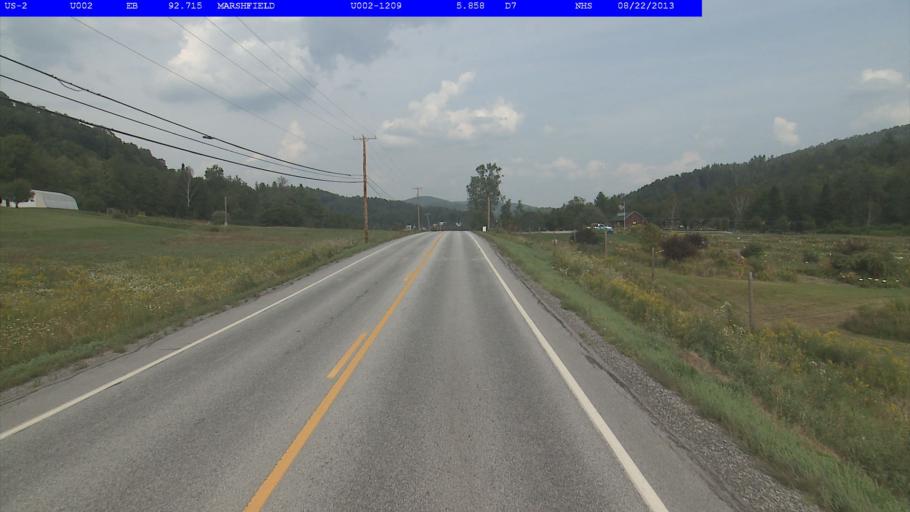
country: US
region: Vermont
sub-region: Caledonia County
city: Hardwick
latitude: 44.3458
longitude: -72.3637
